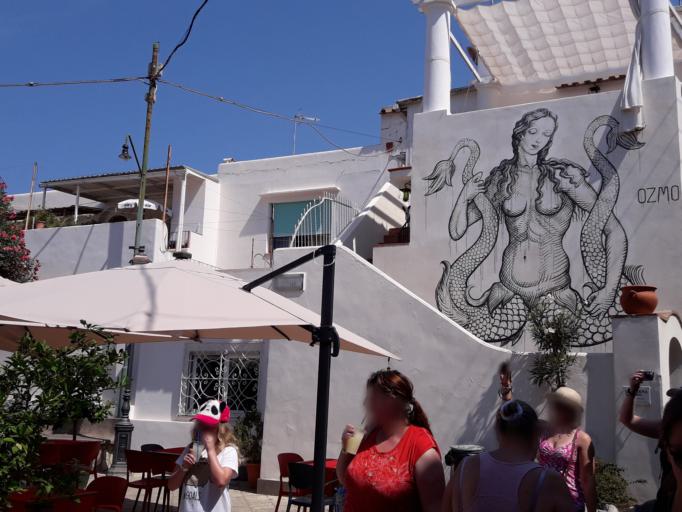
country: IT
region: Campania
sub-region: Provincia di Napoli
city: Anacapri
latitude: 40.5551
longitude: 14.2191
